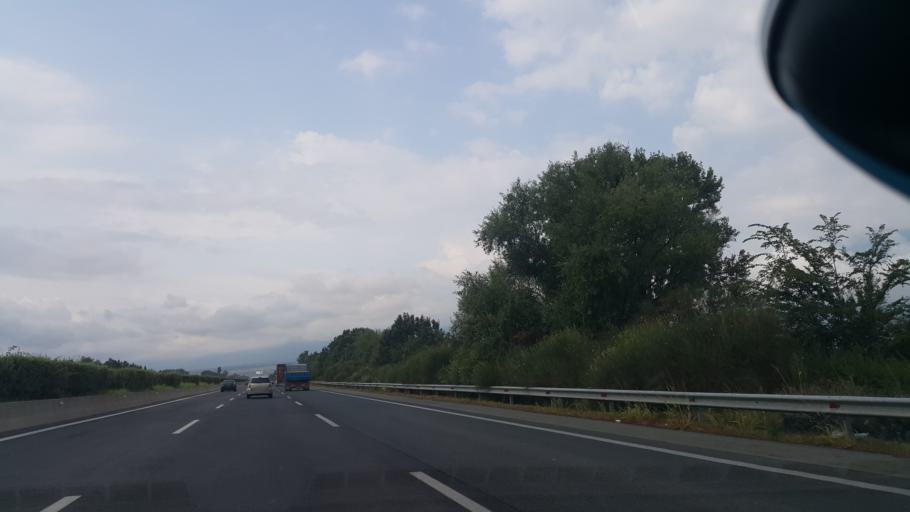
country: GR
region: Central Macedonia
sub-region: Nomos Pierias
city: Dion
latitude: 40.1772
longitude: 22.5497
